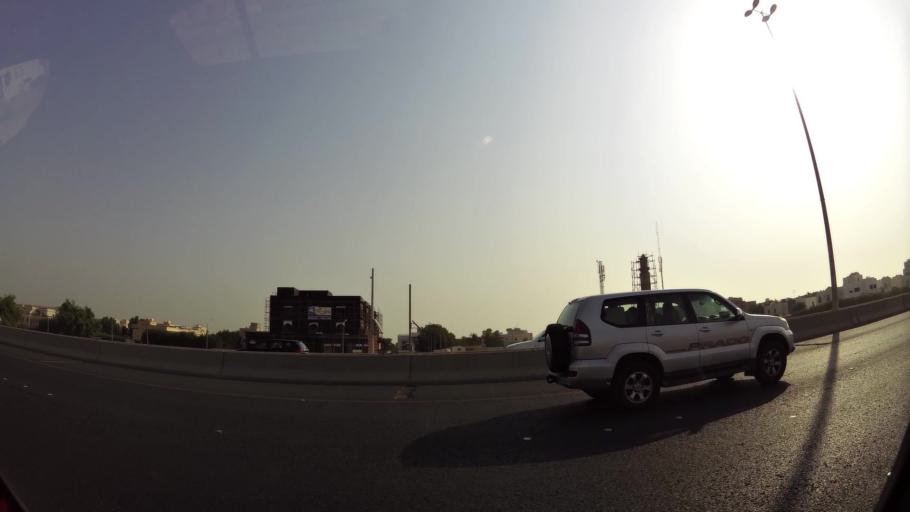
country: KW
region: Al Ahmadi
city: Al Fintas
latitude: 29.1900
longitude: 48.1101
